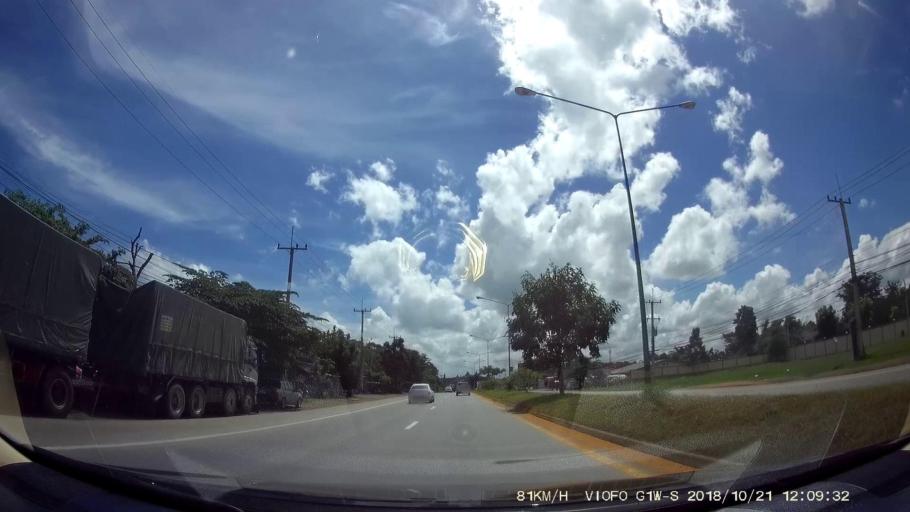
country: TH
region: Chaiyaphum
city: Chatturat
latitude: 15.4199
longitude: 101.8327
